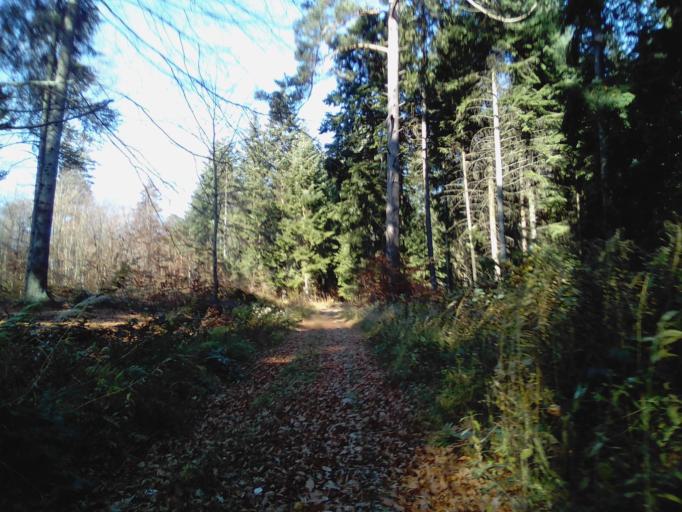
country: PL
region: Subcarpathian Voivodeship
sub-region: Powiat krosnienski
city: Leki
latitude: 49.8295
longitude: 21.6845
